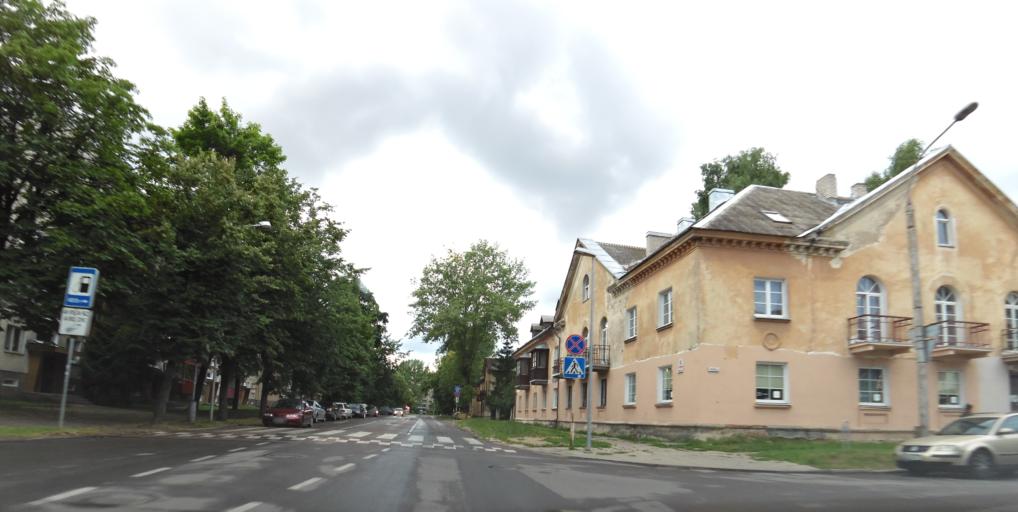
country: LT
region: Vilnius County
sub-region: Vilnius
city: Vilnius
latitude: 54.7080
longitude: 25.2886
